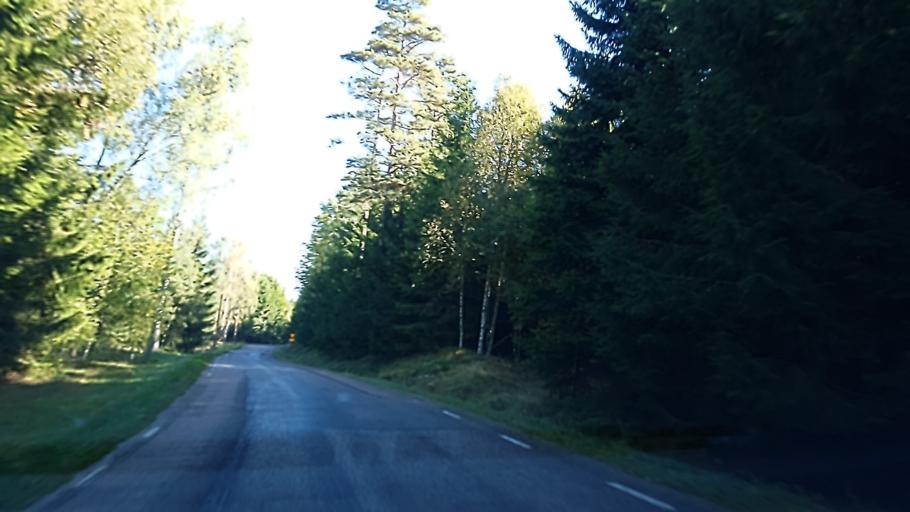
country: SE
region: Kronoberg
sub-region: Ljungby Kommun
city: Ljungby
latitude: 56.8234
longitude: 14.0513
